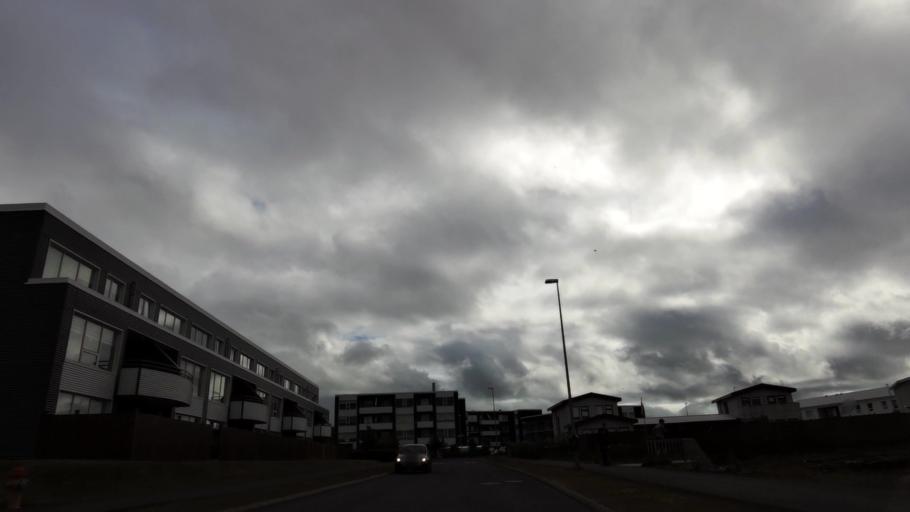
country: IS
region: Capital Region
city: Hafnarfjoerdur
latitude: 64.0496
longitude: -21.9773
